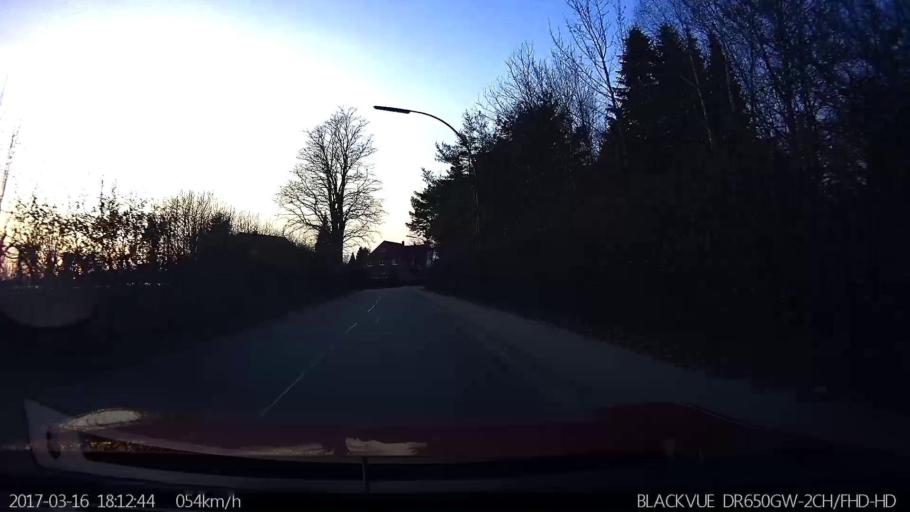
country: DE
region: Schleswig-Holstein
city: Halstenbek
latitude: 53.6363
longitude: 9.8567
